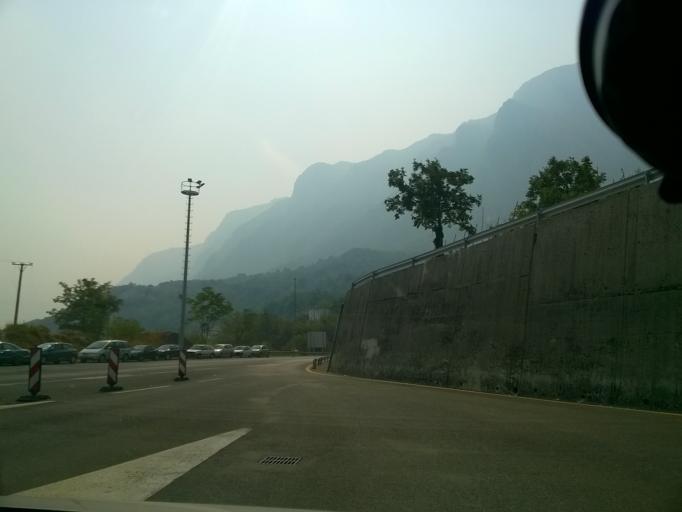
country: ME
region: Bar
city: Sutomore
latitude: 42.2002
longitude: 19.0522
